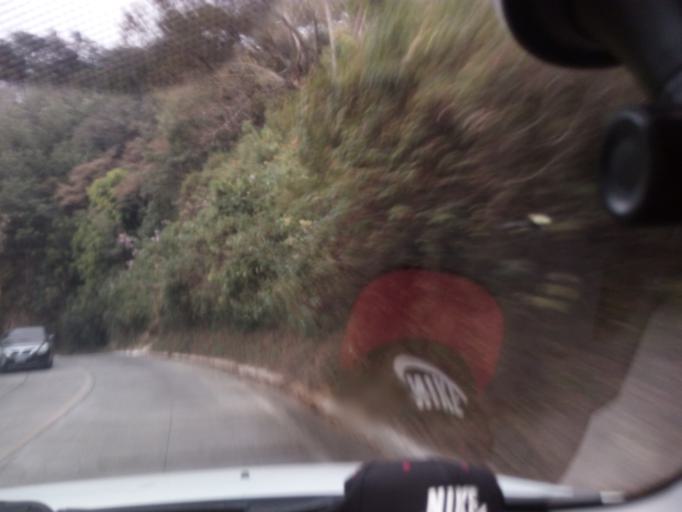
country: GT
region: Sacatepequez
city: Antigua Guatemala
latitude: 14.5732
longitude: -90.7200
